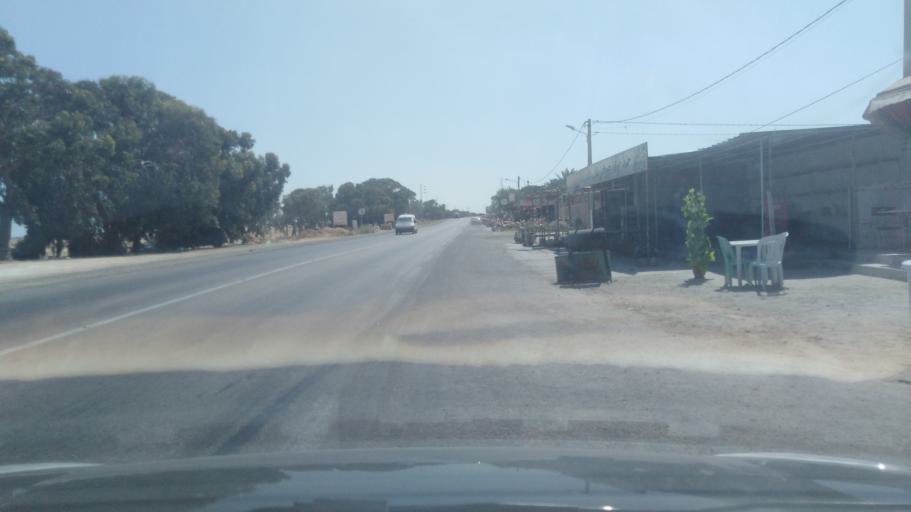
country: TN
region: Qabis
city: Gabes
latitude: 33.9591
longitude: 10.0175
